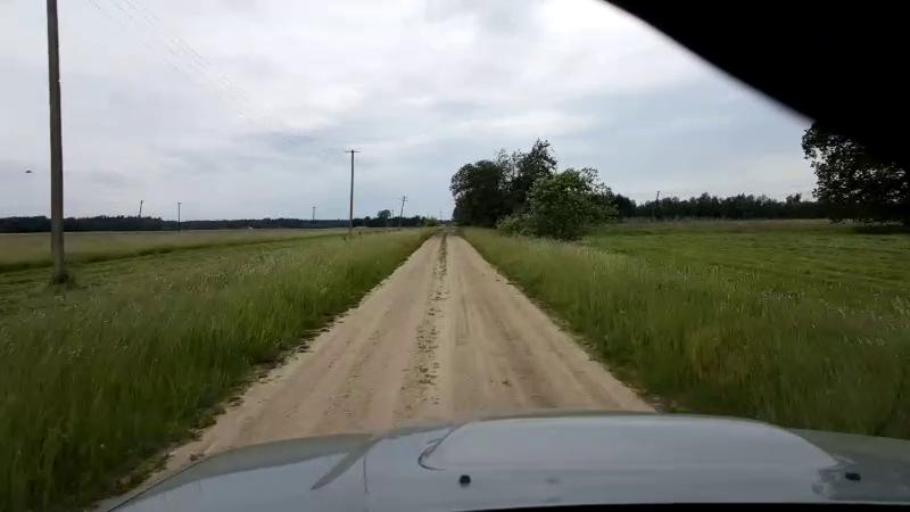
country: EE
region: Paernumaa
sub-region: Halinga vald
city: Parnu-Jaagupi
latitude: 58.5322
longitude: 24.6114
